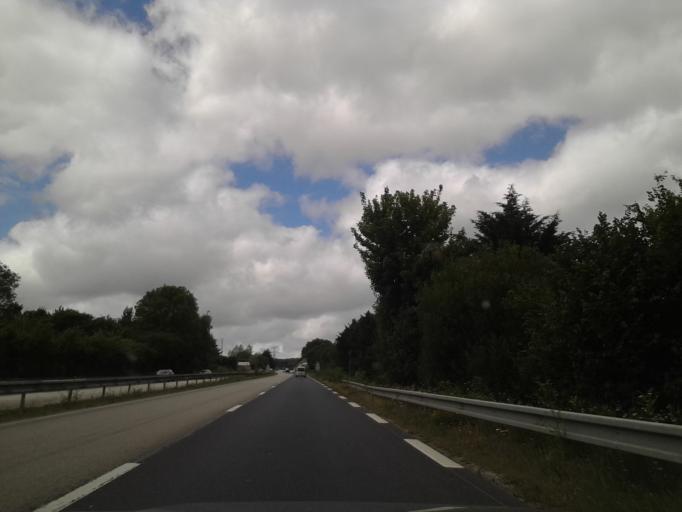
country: FR
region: Lower Normandy
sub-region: Departement de la Manche
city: Brix
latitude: 49.5403
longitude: -1.5433
